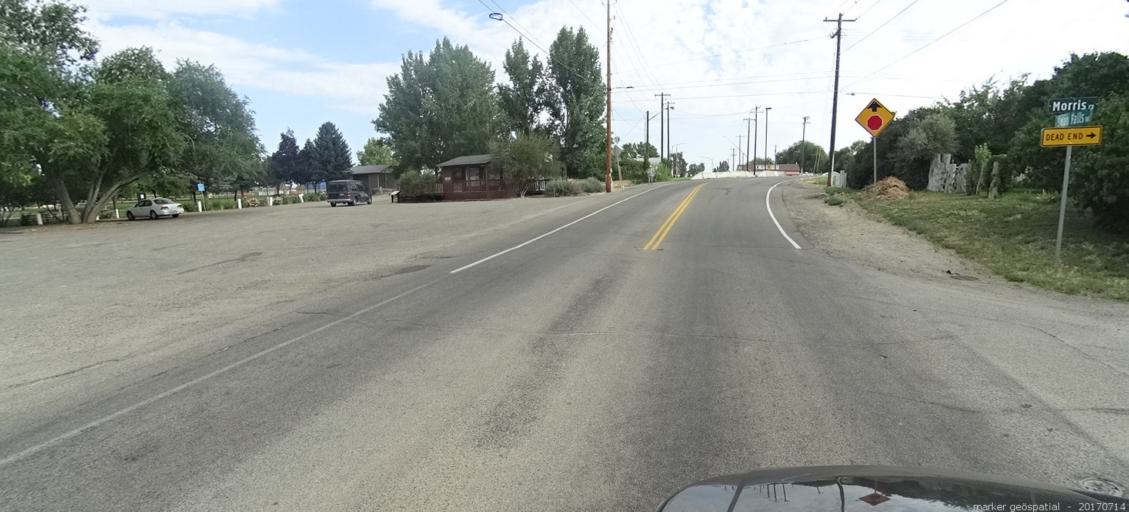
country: US
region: Idaho
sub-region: Ada County
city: Kuna
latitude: 43.4880
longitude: -116.4138
